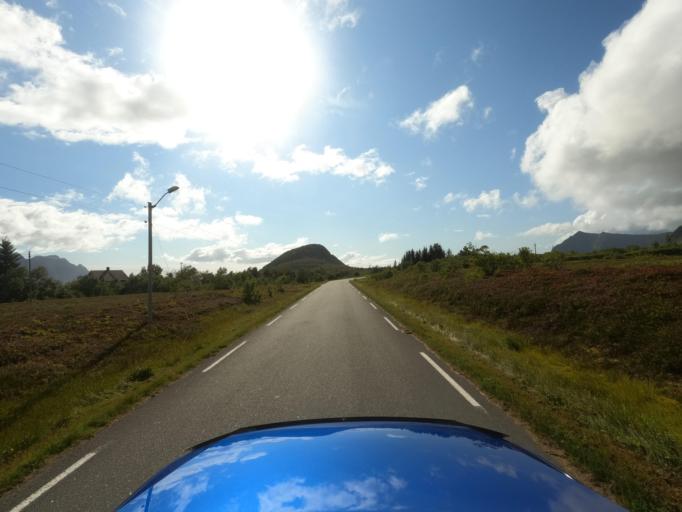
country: NO
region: Nordland
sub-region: Vagan
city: Kabelvag
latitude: 68.2361
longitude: 14.1151
